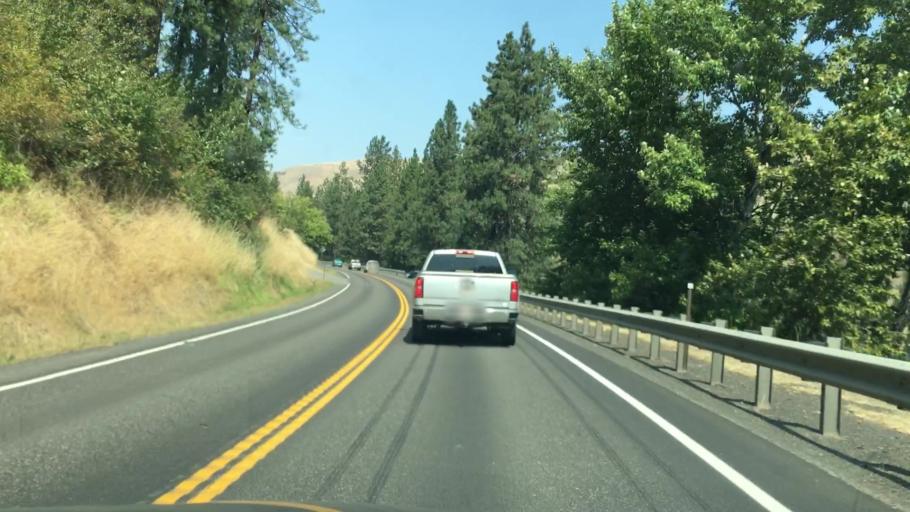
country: US
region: Idaho
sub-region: Nez Perce County
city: Lapwai
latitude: 46.5107
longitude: -116.5802
